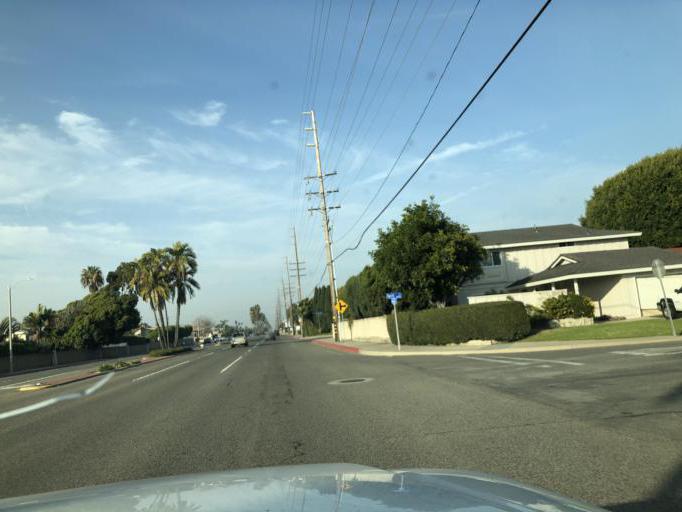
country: US
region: California
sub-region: Orange County
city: Costa Mesa
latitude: 33.6557
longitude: -117.9535
